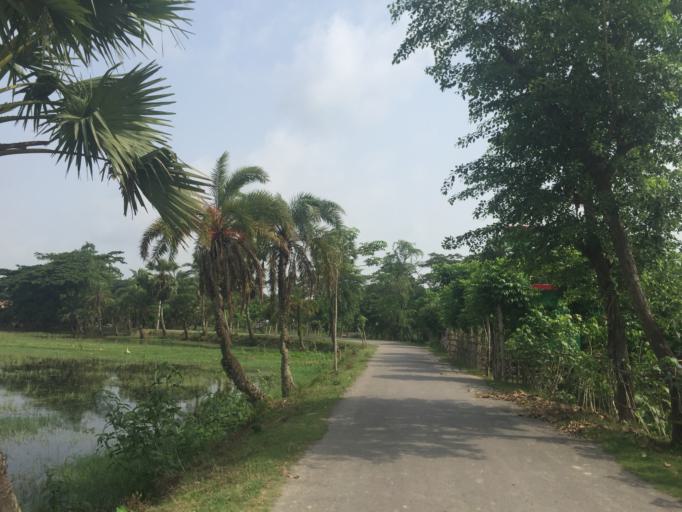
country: BD
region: Barisal
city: Mathba
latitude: 22.2127
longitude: 89.9218
